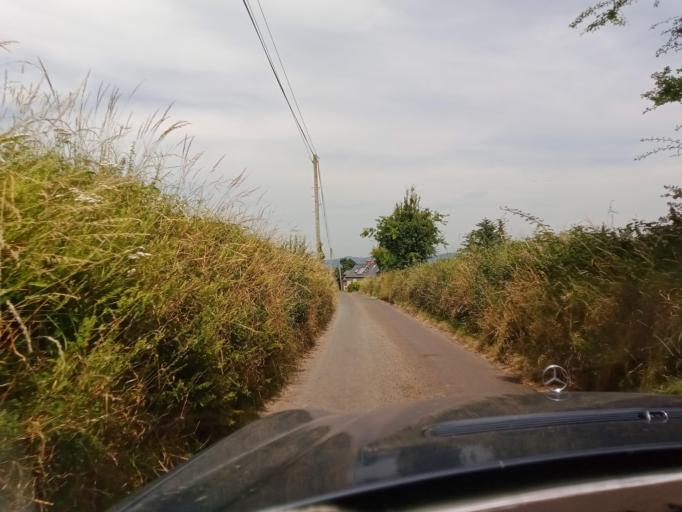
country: IE
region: Leinster
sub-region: Kilkenny
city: Mooncoin
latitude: 52.2684
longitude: -7.2155
